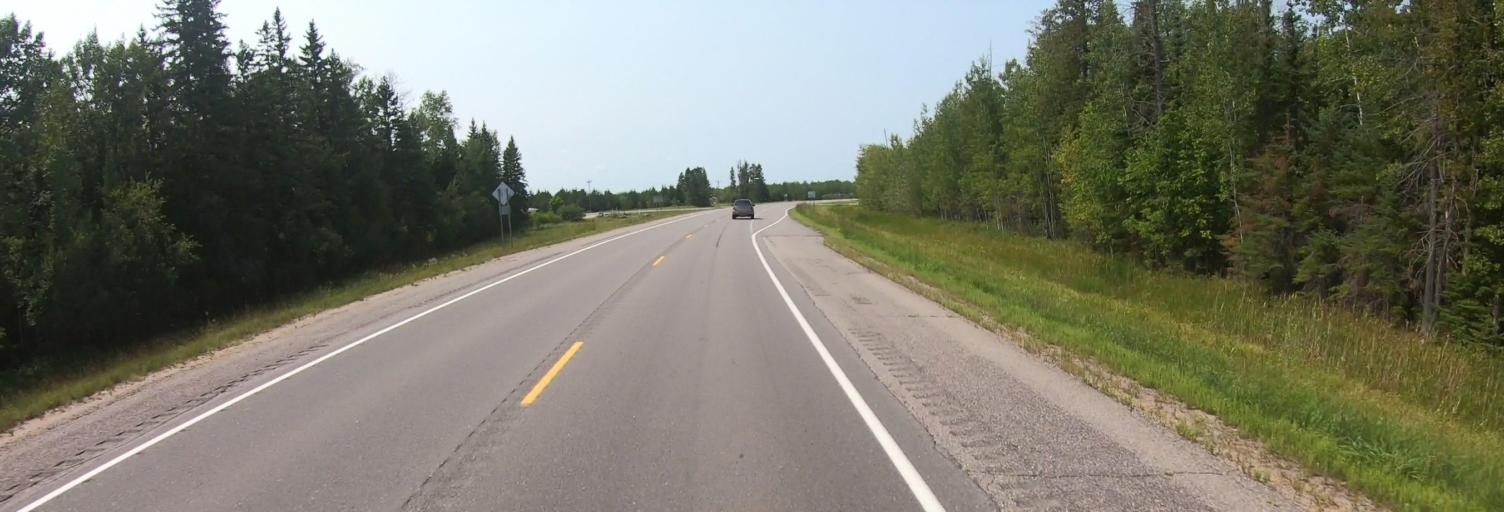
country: US
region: Minnesota
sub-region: Koochiching County
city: International Falls
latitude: 48.5355
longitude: -93.4805
